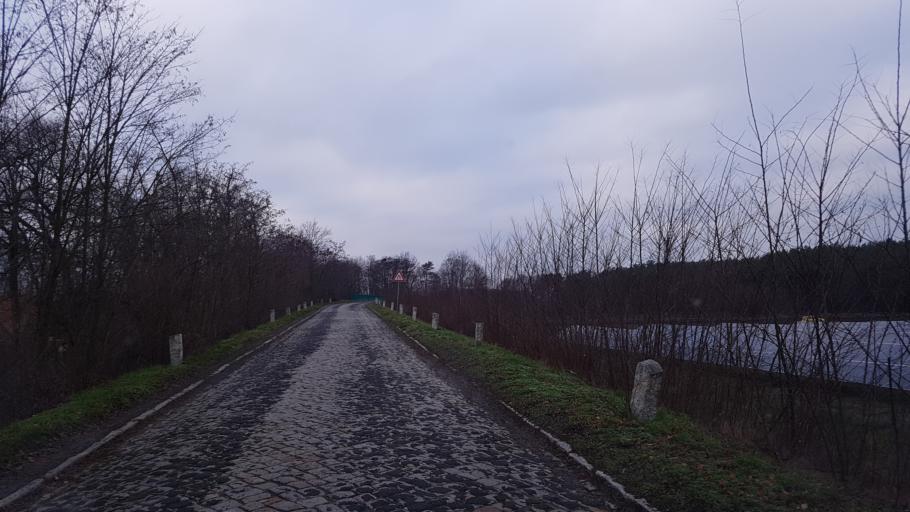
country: DE
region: Brandenburg
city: Schipkau
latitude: 51.5494
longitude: 13.9135
